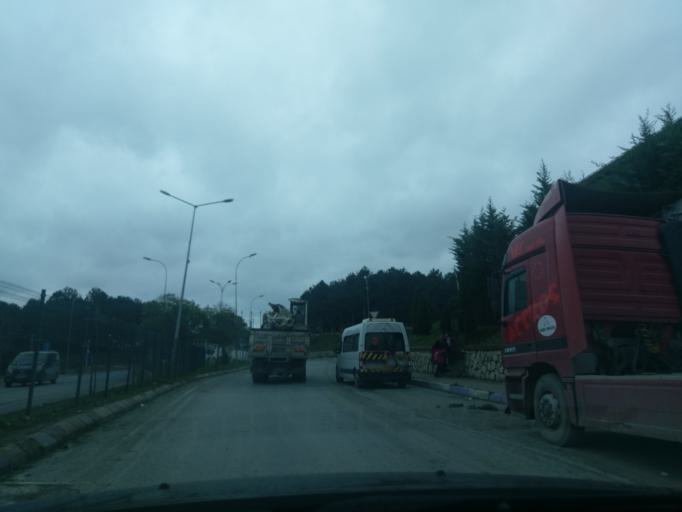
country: TR
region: Istanbul
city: Catalca
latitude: 41.1474
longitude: 28.4628
